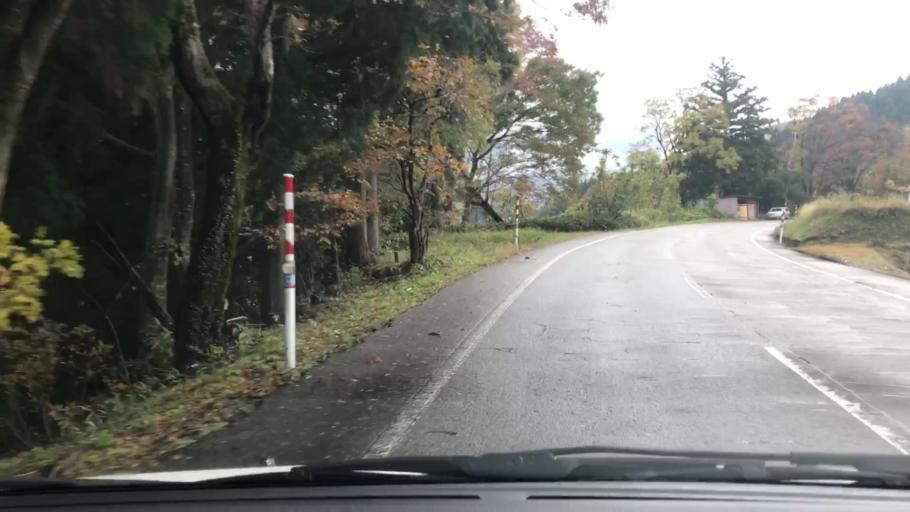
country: JP
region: Toyama
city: Kamiichi
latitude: 36.5859
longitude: 137.3229
